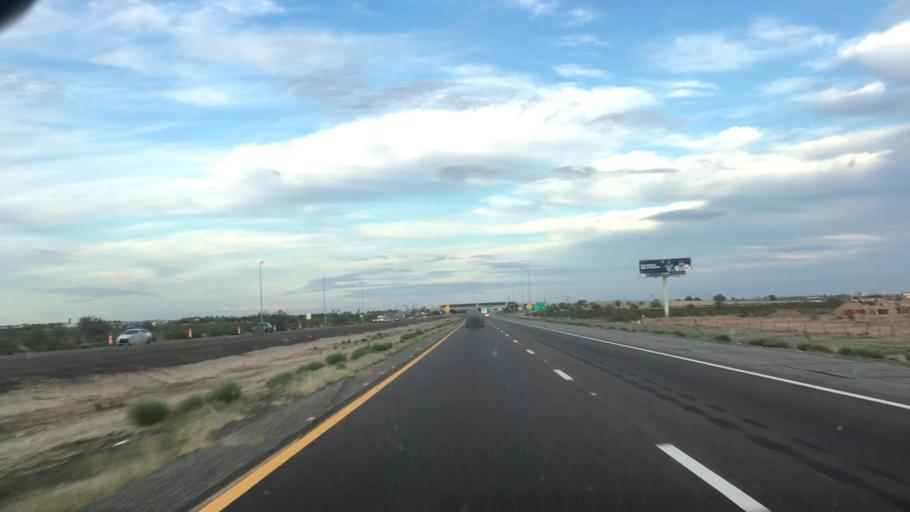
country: US
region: Arizona
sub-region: Maricopa County
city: Buckeye
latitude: 33.4574
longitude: -112.5141
